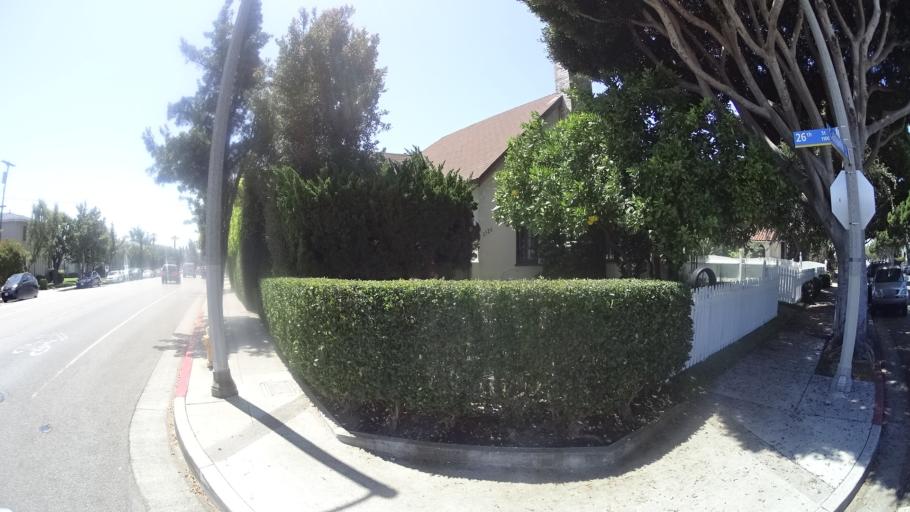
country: US
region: California
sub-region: Los Angeles County
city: Santa Monica
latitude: 34.0373
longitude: -118.4792
